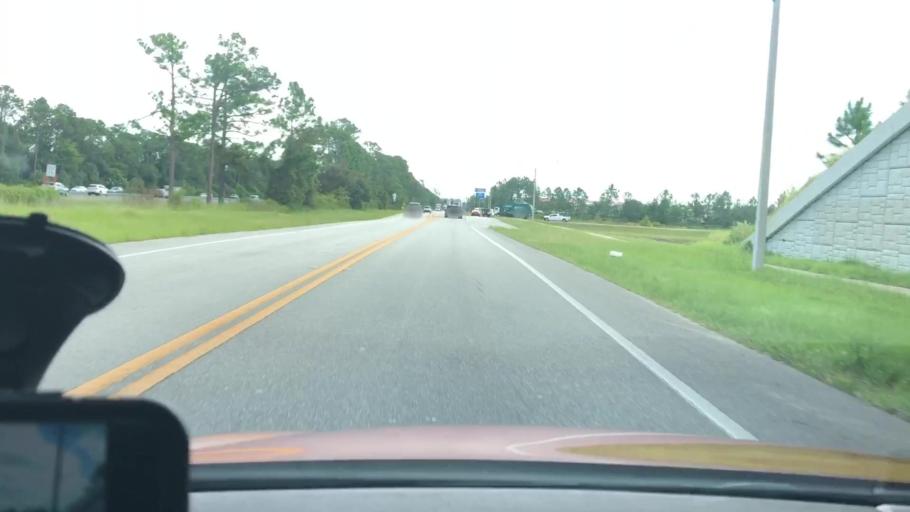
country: US
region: Florida
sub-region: Volusia County
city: Daytona Beach
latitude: 29.1975
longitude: -81.0960
